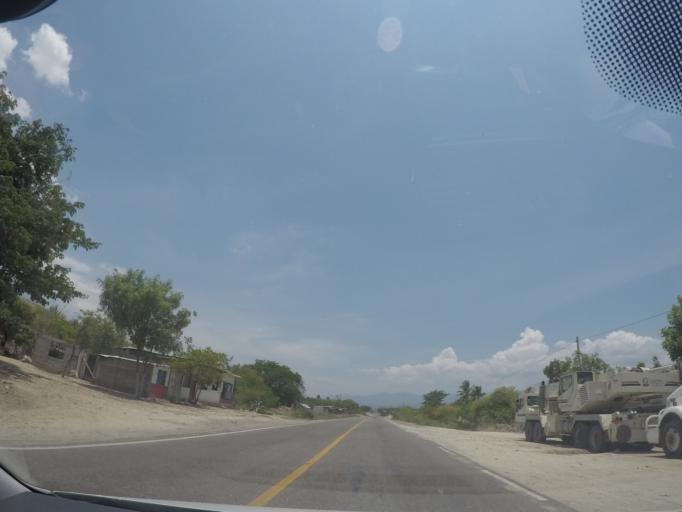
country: MX
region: Oaxaca
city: Santa Maria Jalapa del Marques
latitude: 16.4394
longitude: -95.5048
